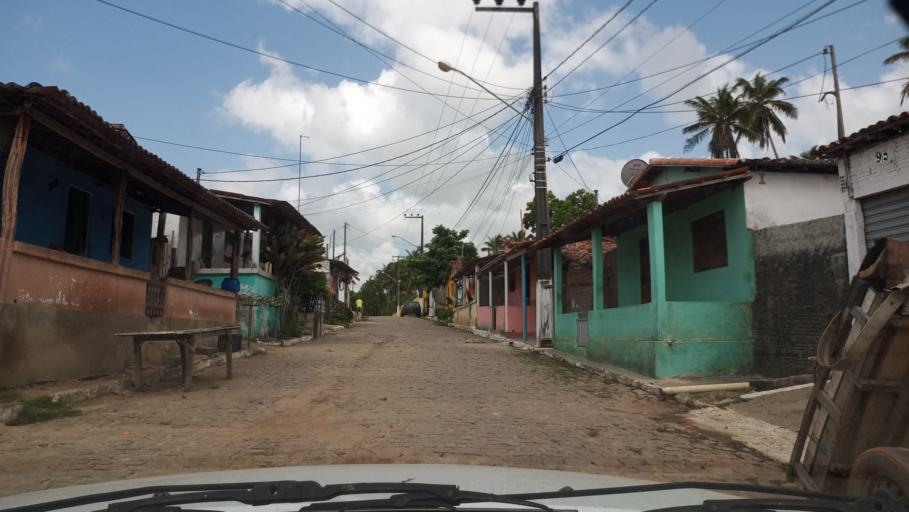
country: BR
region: Rio Grande do Norte
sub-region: Ares
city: Ares
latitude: -6.2363
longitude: -35.1363
